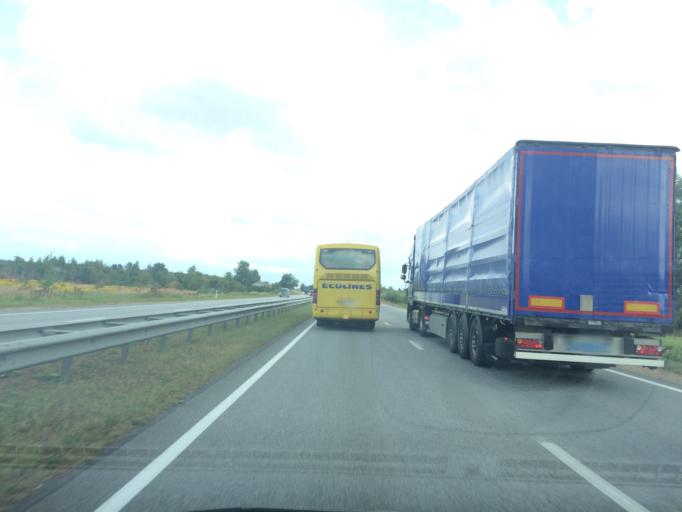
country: LV
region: Salaspils
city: Salaspils
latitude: 56.8479
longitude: 24.3520
